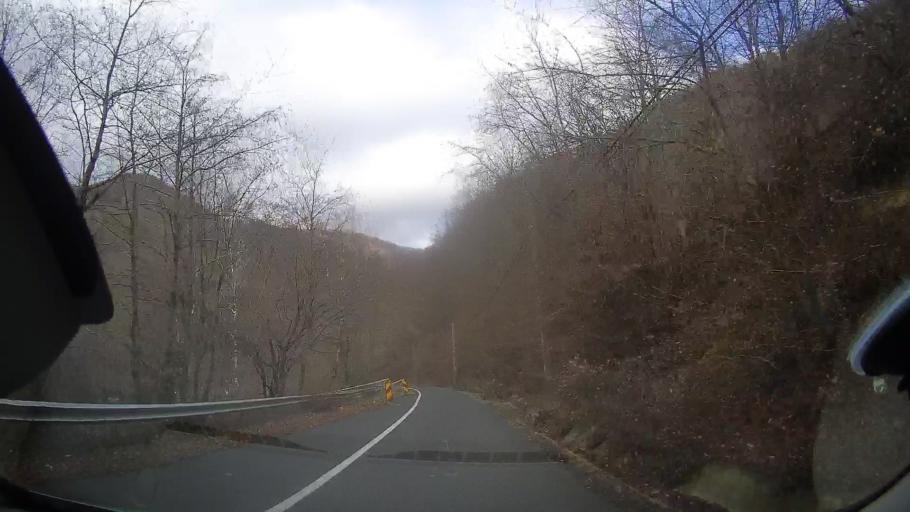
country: RO
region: Cluj
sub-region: Comuna Valea Ierii
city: Valea Ierii
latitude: 46.6882
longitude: 23.3072
